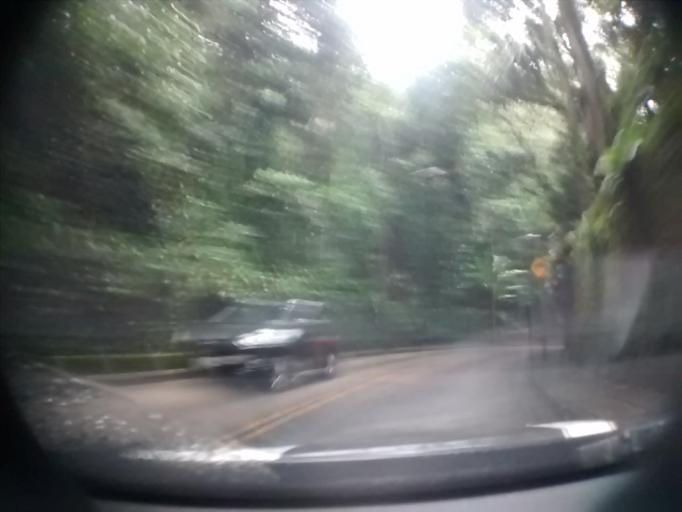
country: BR
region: Rio de Janeiro
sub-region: Rio De Janeiro
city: Rio de Janeiro
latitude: -22.9834
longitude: -43.2764
